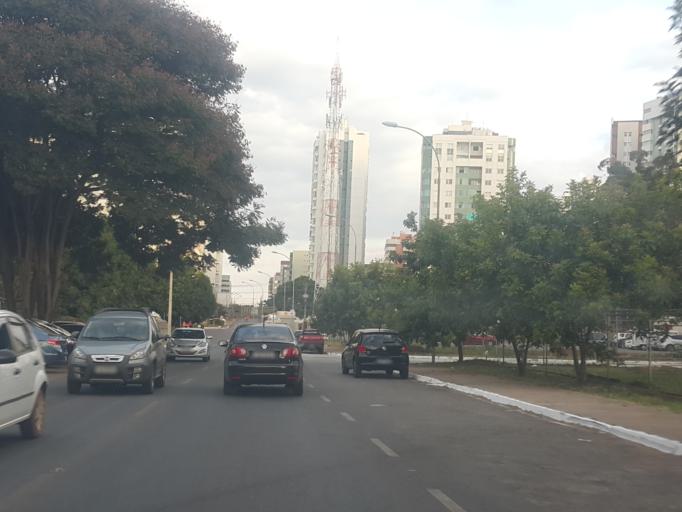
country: BR
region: Federal District
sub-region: Brasilia
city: Brasilia
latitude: -15.8364
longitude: -48.0254
